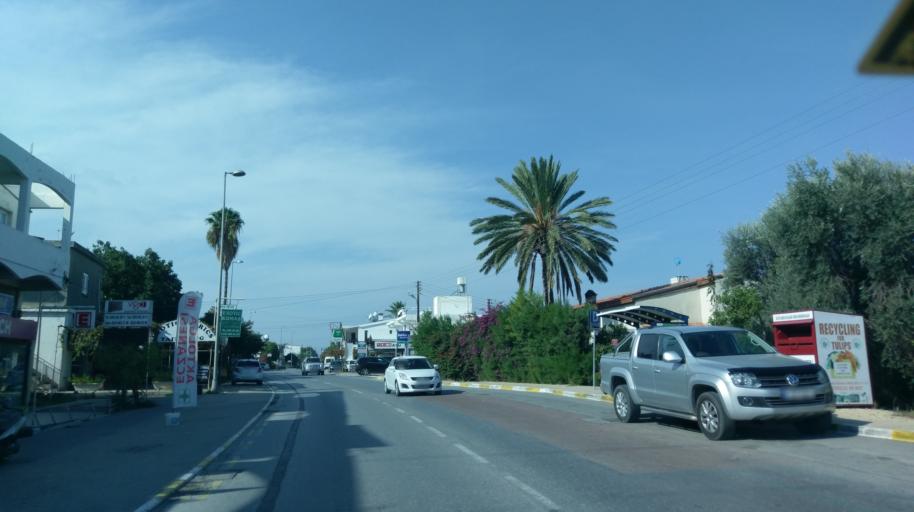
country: CY
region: Keryneia
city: Kyrenia
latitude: 35.3424
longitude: 33.2711
